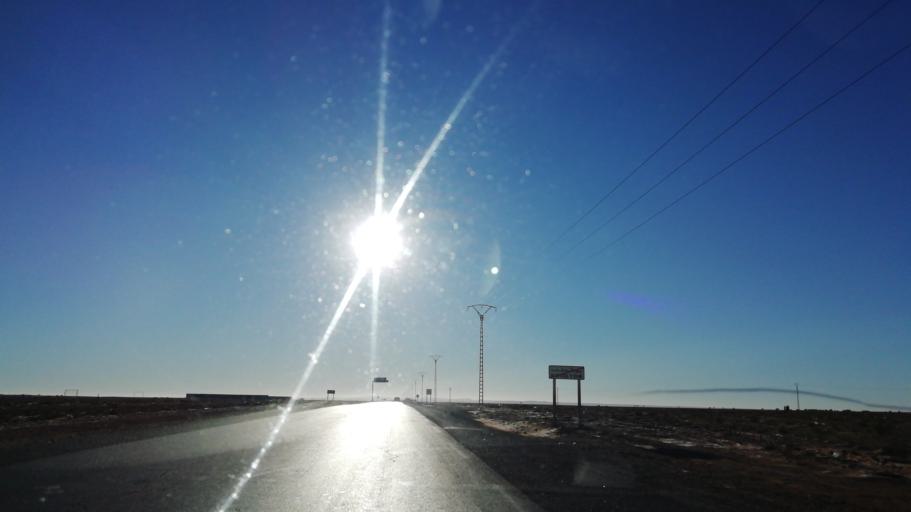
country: DZ
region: Saida
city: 'Ain el Hadjar
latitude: 34.0219
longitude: 0.1026
